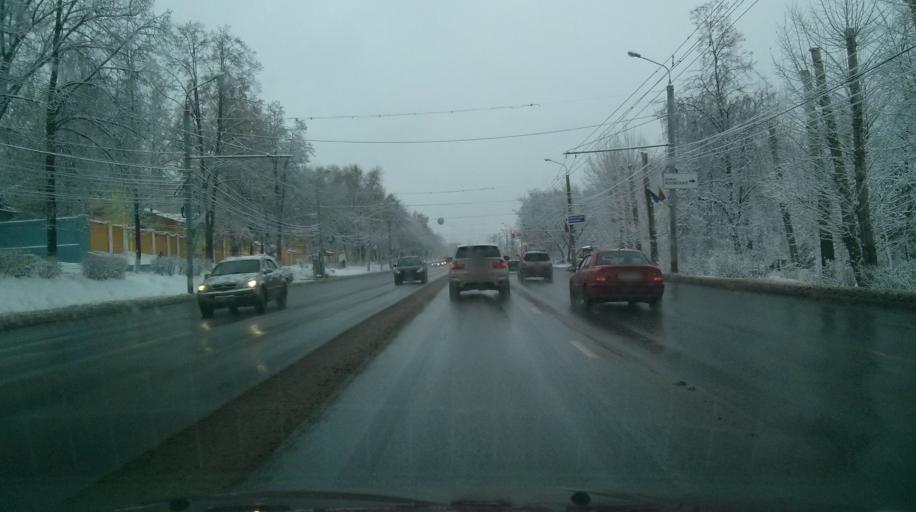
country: RU
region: Nizjnij Novgorod
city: Nizhniy Novgorod
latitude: 56.2501
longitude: 43.9677
